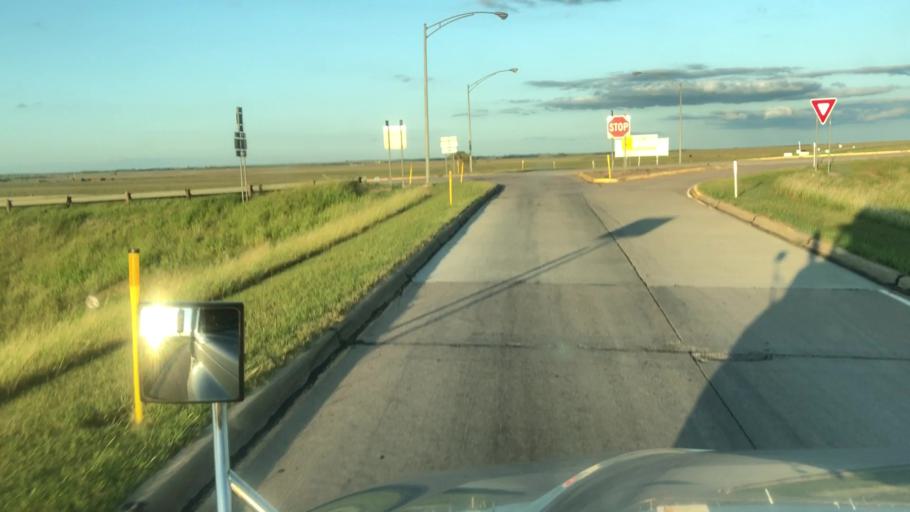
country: US
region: Oklahoma
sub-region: Noble County
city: Perry
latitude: 36.3854
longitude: -97.0683
